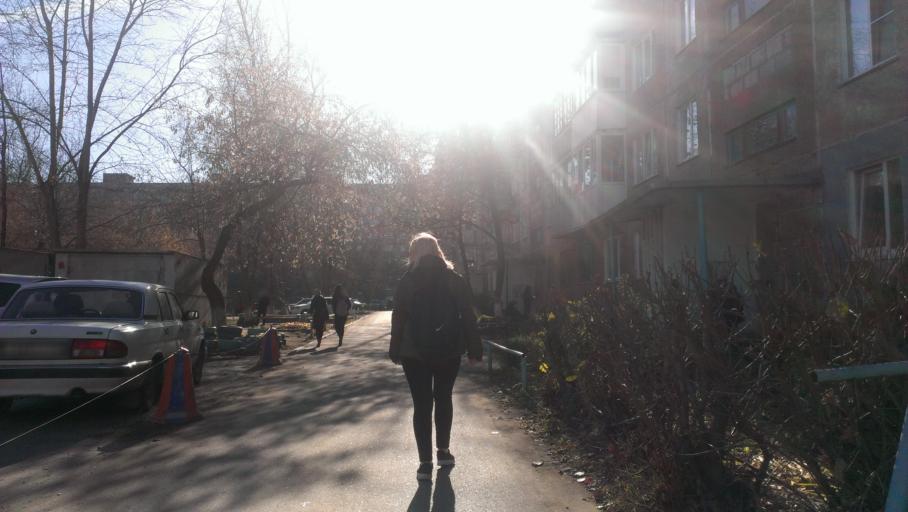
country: RU
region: Altai Krai
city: Novosilikatnyy
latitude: 53.3486
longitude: 83.6767
